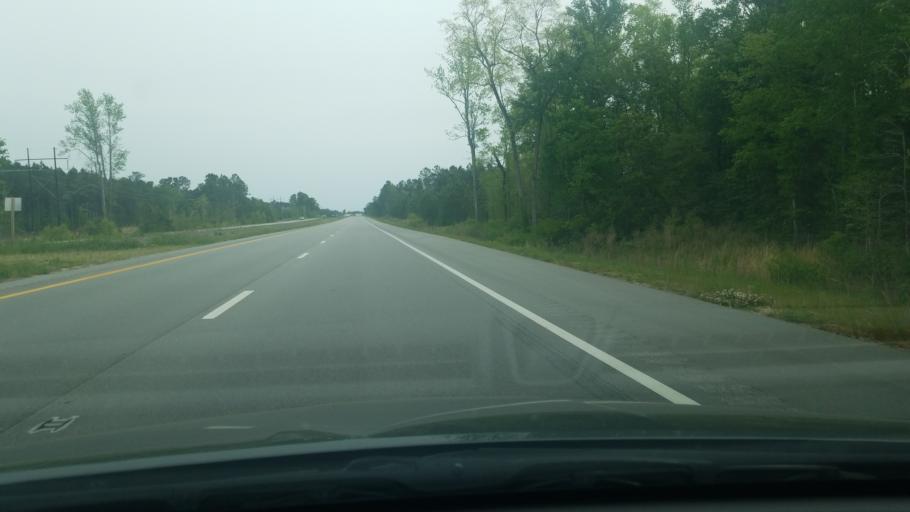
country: US
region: North Carolina
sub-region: Craven County
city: River Bend
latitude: 35.0394
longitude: -77.2220
